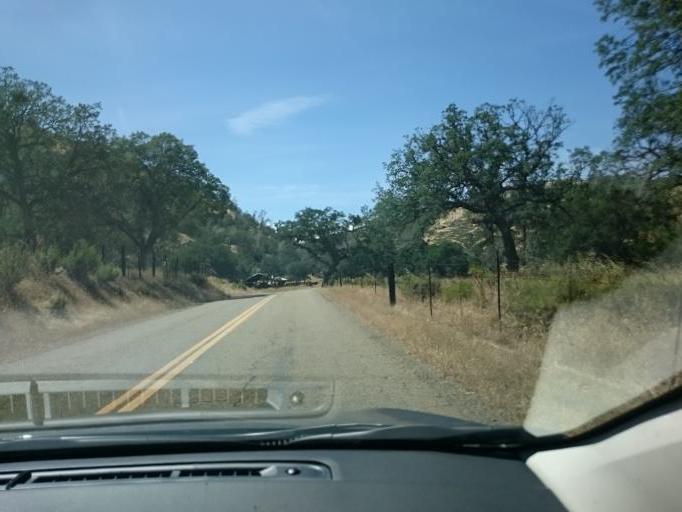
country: US
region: California
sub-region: Stanislaus County
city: Patterson
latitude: 37.4188
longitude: -121.3570
